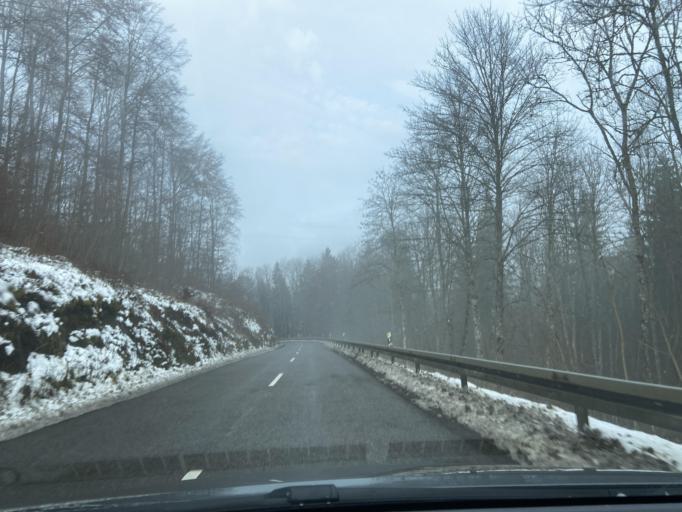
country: DE
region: Baden-Wuerttemberg
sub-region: Tuebingen Region
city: Hettingen
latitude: 48.2150
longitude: 9.2382
